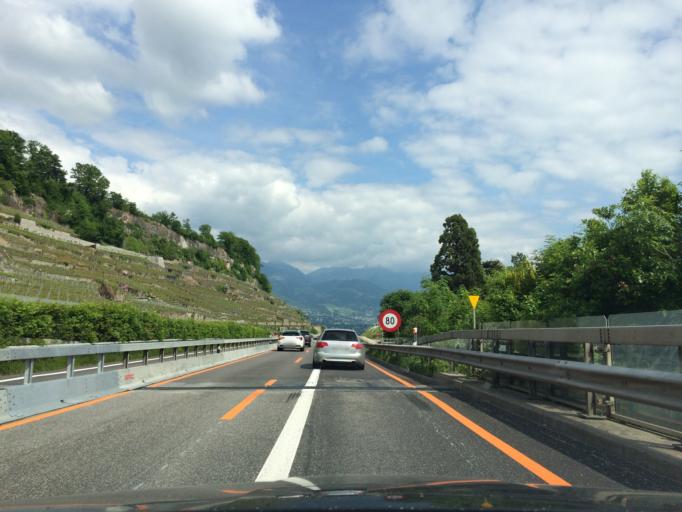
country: CH
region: Vaud
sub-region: Lavaux-Oron District
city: Chexbres
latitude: 46.4766
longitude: 6.7998
